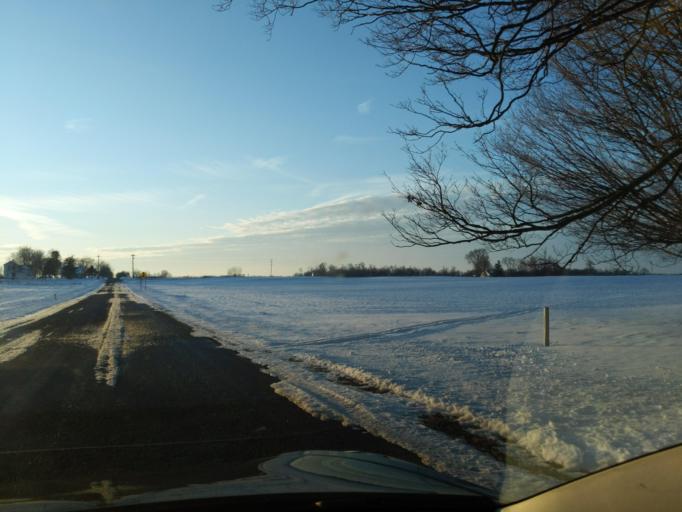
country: US
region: Michigan
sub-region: Ingham County
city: Webberville
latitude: 42.5696
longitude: -84.1888
